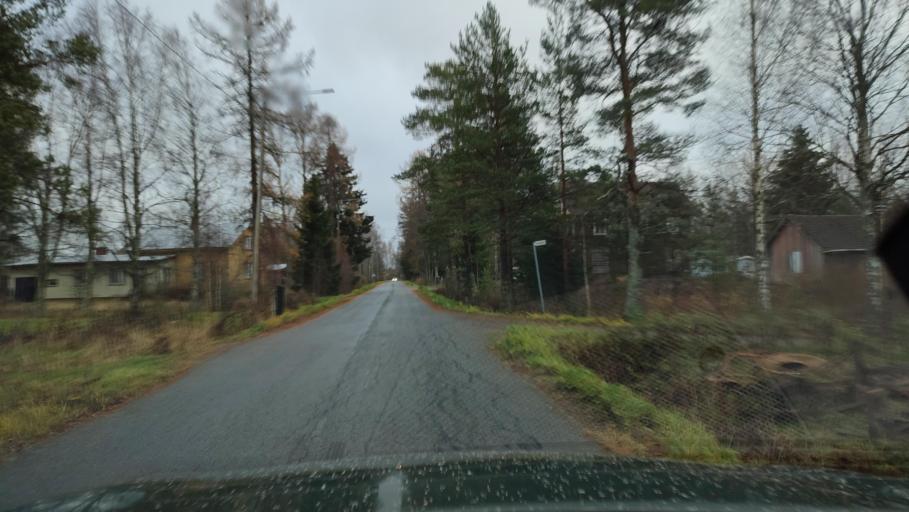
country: FI
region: Southern Ostrobothnia
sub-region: Suupohja
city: Teuva
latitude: 62.4567
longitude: 21.6000
